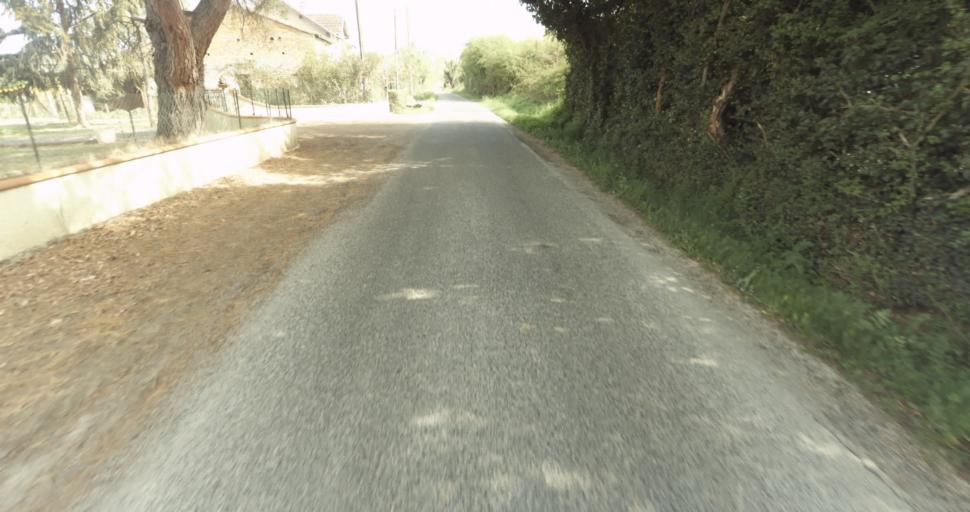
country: FR
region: Midi-Pyrenees
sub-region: Departement du Tarn-et-Garonne
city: Moissac
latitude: 44.0753
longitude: 1.0897
